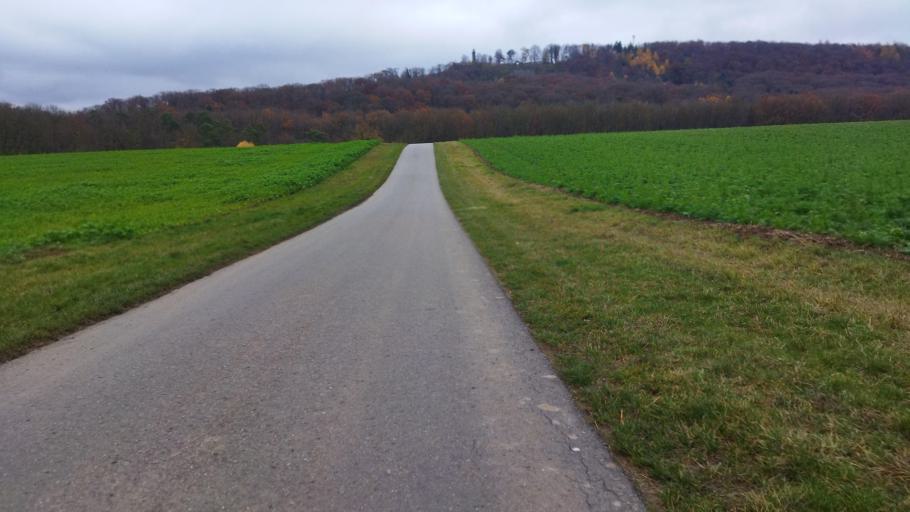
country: DE
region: Baden-Wuerttemberg
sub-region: Regierungsbezirk Stuttgart
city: Leingarten
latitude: 49.1363
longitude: 9.1057
